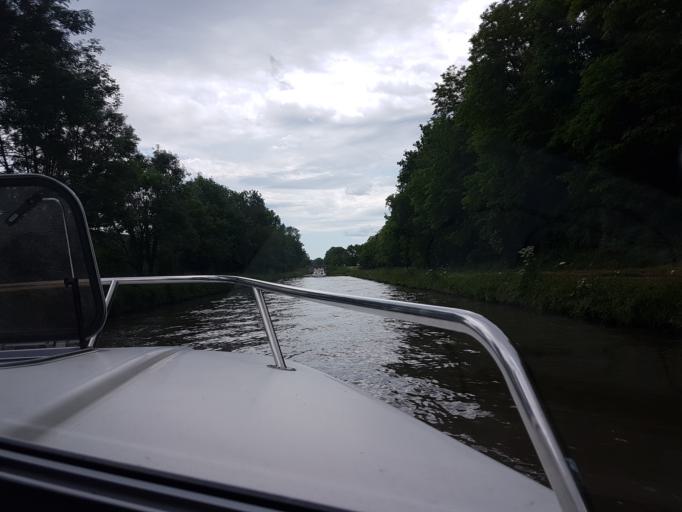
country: FR
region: Bourgogne
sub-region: Departement de la Nievre
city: Clamecy
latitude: 47.4854
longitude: 3.5243
